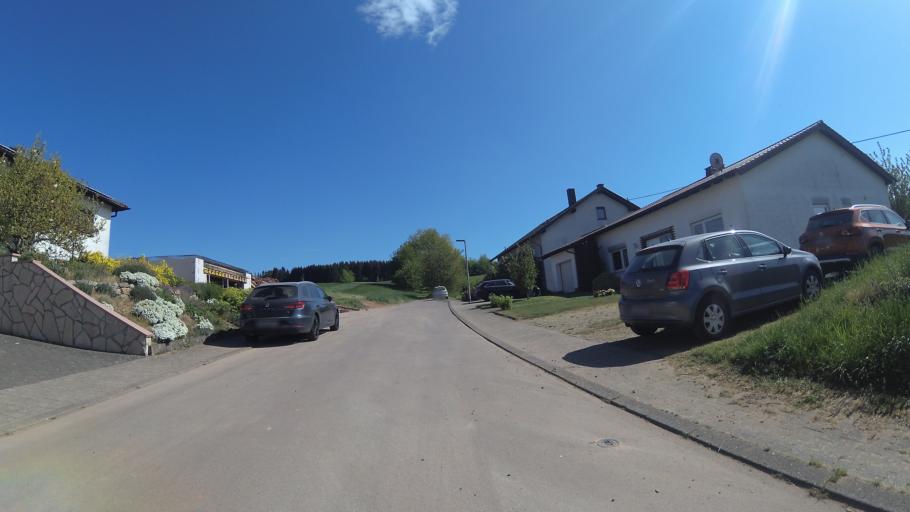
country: DE
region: Saarland
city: Mainzweiler
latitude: 49.4117
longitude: 7.1197
